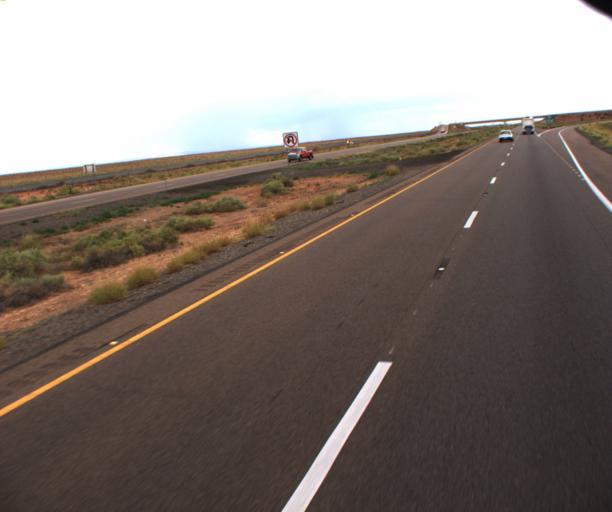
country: US
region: Arizona
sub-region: Coconino County
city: LeChee
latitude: 35.0659
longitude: -110.8294
